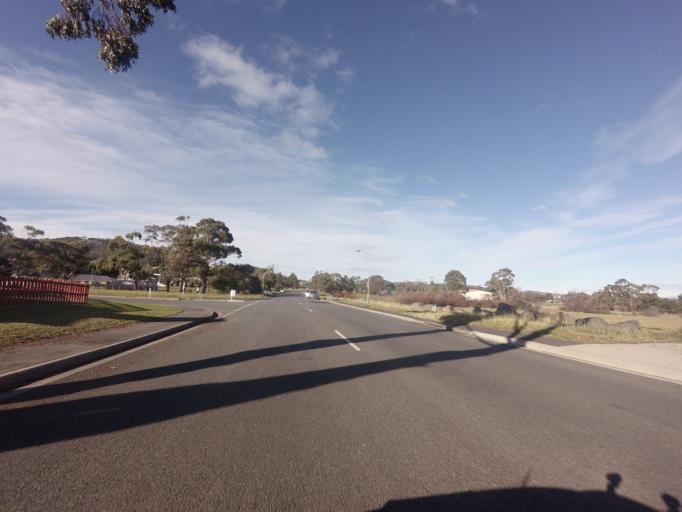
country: AU
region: Tasmania
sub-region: Clarence
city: Rokeby
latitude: -42.8942
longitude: 147.4440
